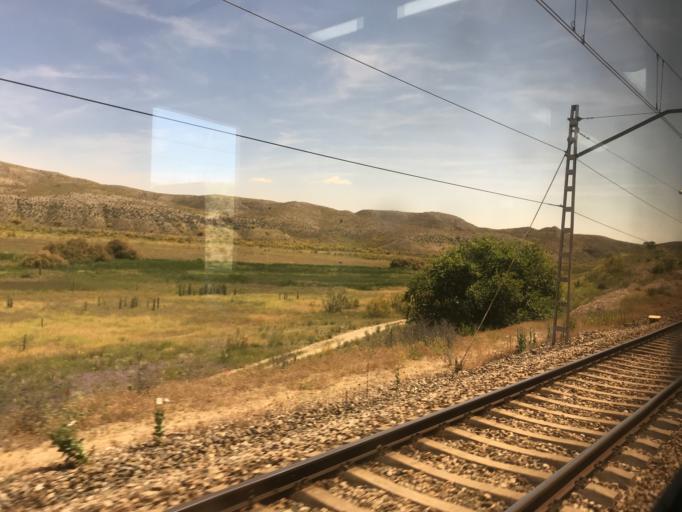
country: ES
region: Madrid
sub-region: Provincia de Madrid
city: Ciempozuelos
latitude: 40.1712
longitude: -3.6217
